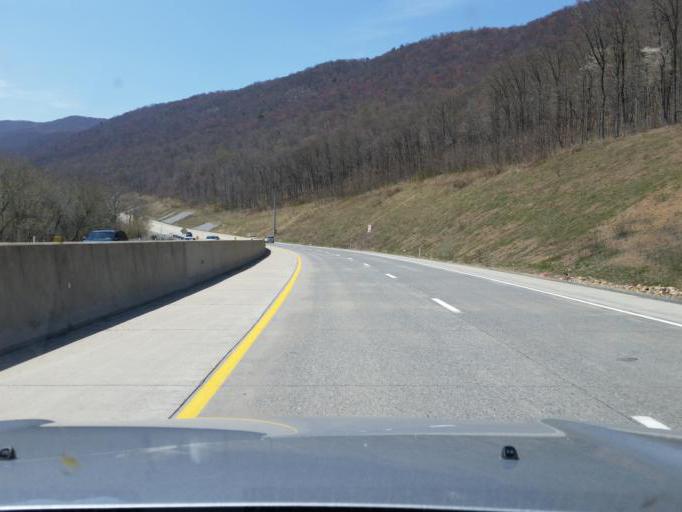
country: US
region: Pennsylvania
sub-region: Juniata County
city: Mifflintown
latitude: 40.6113
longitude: -77.4437
